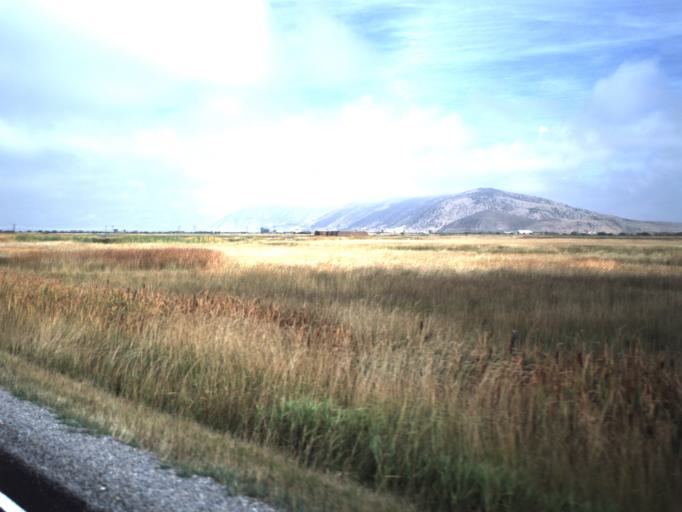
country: US
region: Utah
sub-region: Rich County
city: Randolph
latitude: 41.5076
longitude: -111.1278
